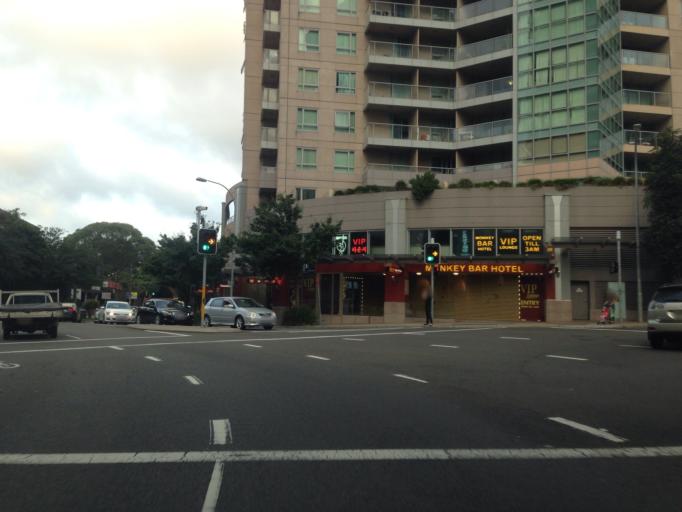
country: AU
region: New South Wales
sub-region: Willoughby
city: Chatswood
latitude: -33.7955
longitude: 151.1810
